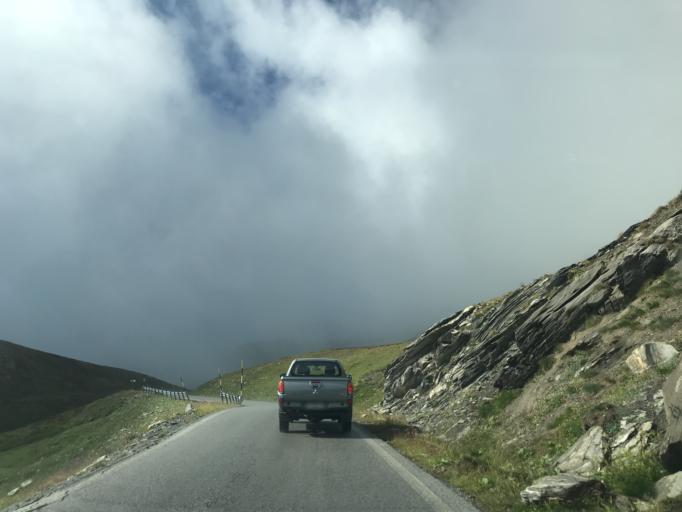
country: IT
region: Piedmont
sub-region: Provincia di Cuneo
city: Pontechianale
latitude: 44.6755
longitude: 6.9911
